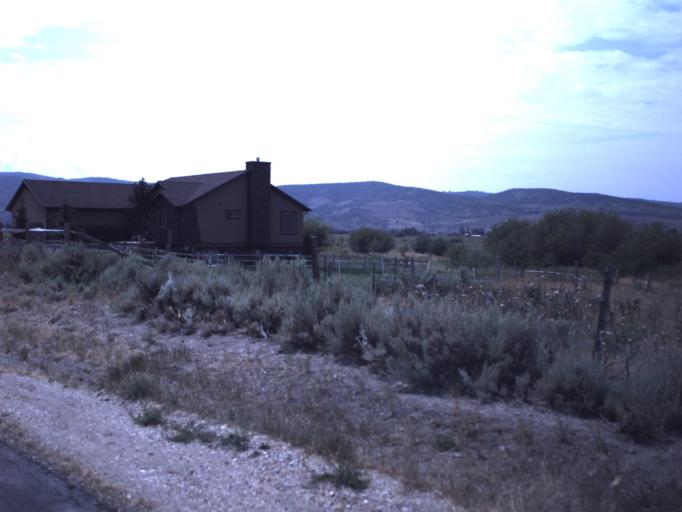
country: US
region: Utah
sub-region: Summit County
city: Francis
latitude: 40.6072
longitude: -111.2563
